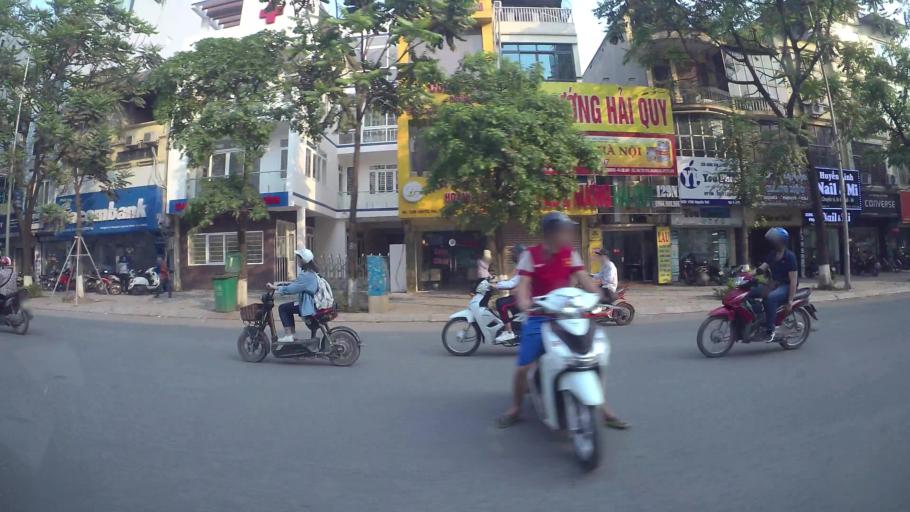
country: VN
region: Ha Noi
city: Thanh Xuan
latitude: 20.9995
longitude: 105.8159
